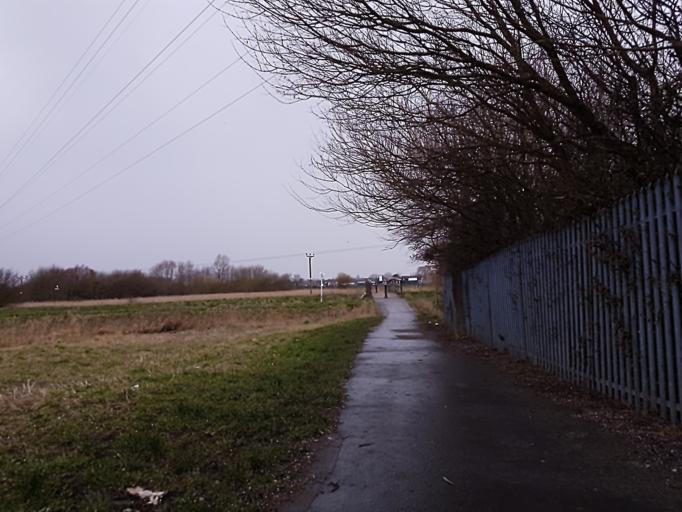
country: GB
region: England
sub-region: North East Lincolnshire
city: Great Coates
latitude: 53.5661
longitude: -0.1207
